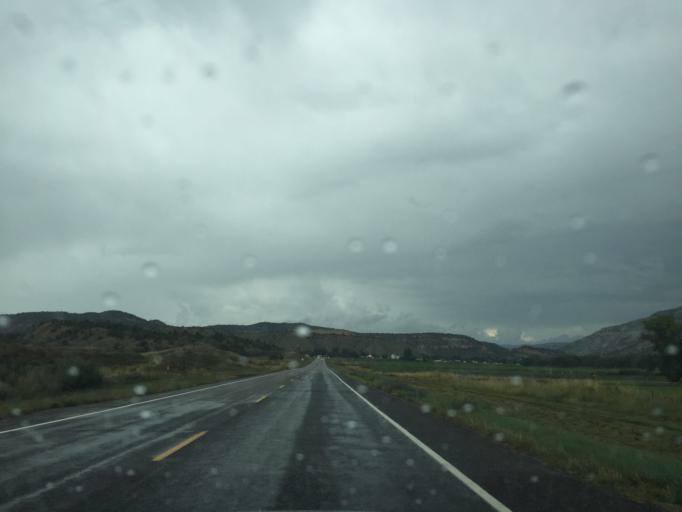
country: US
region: Utah
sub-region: Kane County
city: Kanab
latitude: 37.2628
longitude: -112.6551
